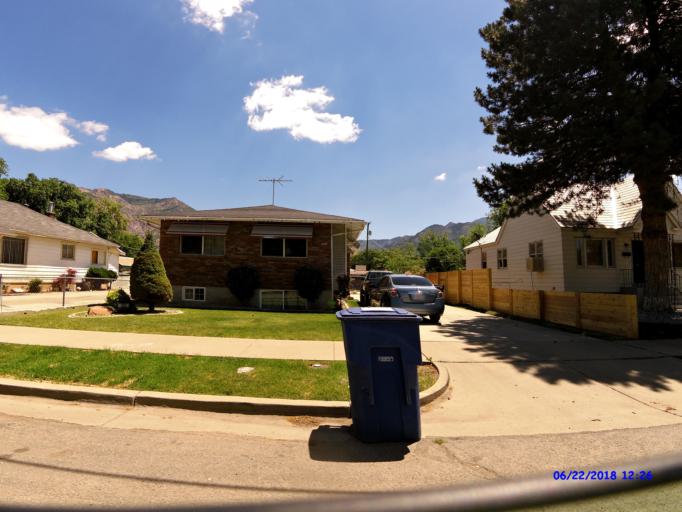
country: US
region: Utah
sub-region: Weber County
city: Ogden
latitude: 41.2412
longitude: -111.9644
